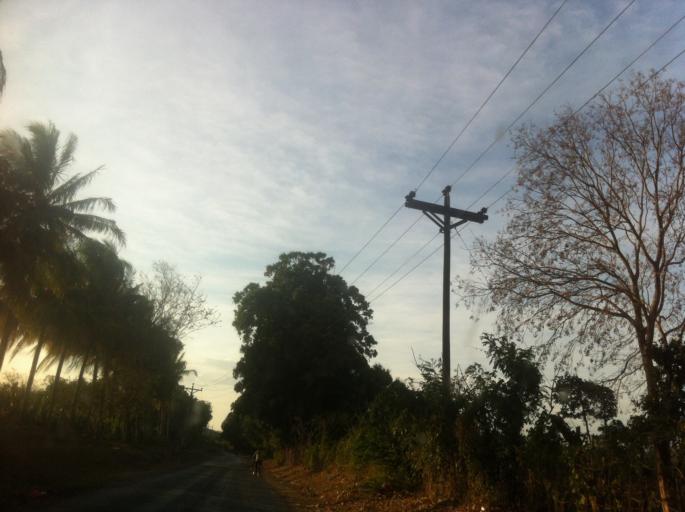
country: NI
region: Rivas
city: Potosi
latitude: 11.4946
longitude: -85.8604
